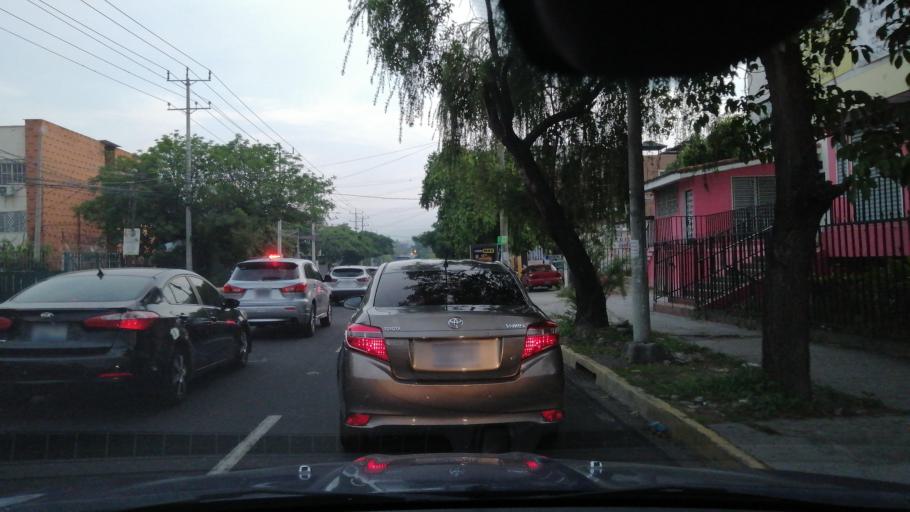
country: SV
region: San Salvador
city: San Salvador
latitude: 13.7063
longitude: -89.2044
